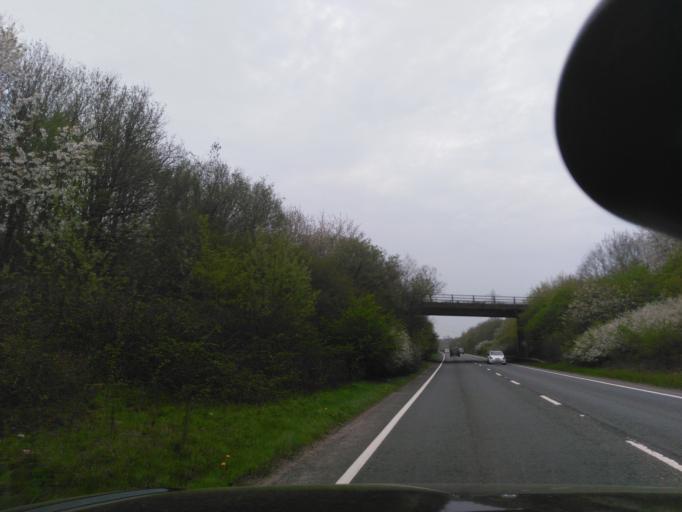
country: GB
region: England
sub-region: Somerset
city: Frome
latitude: 51.2386
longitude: -2.2914
